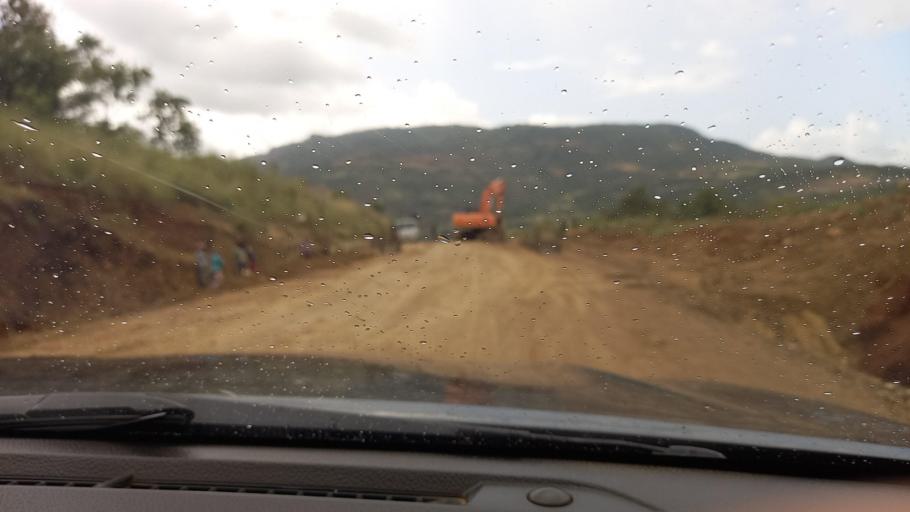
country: ET
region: Southern Nations, Nationalities, and People's Region
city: Mizan Teferi
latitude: 6.1899
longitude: 35.6815
